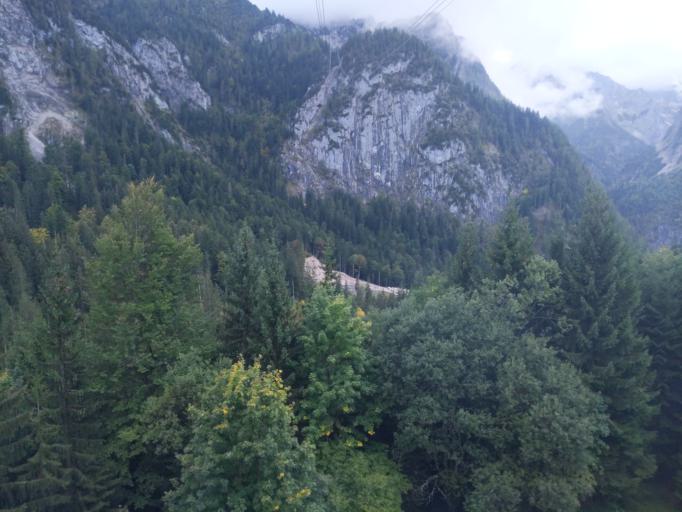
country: DE
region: Bavaria
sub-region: Upper Bavaria
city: Grainau
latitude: 47.4596
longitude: 11.0577
